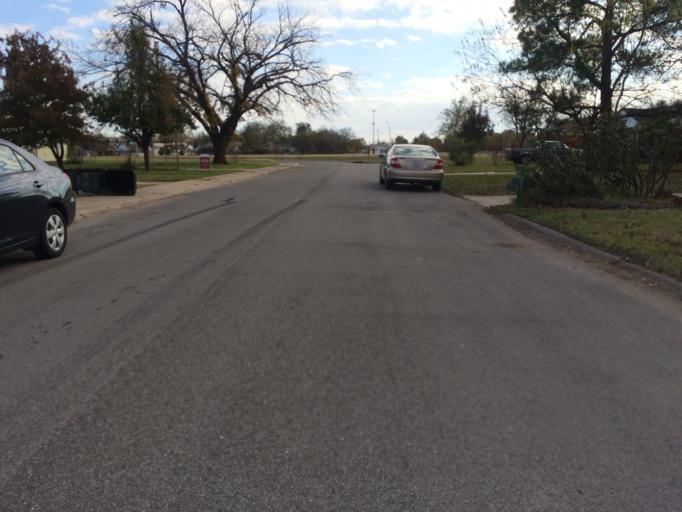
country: US
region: Oklahoma
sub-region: Cleveland County
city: Norman
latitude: 35.2341
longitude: -97.4510
